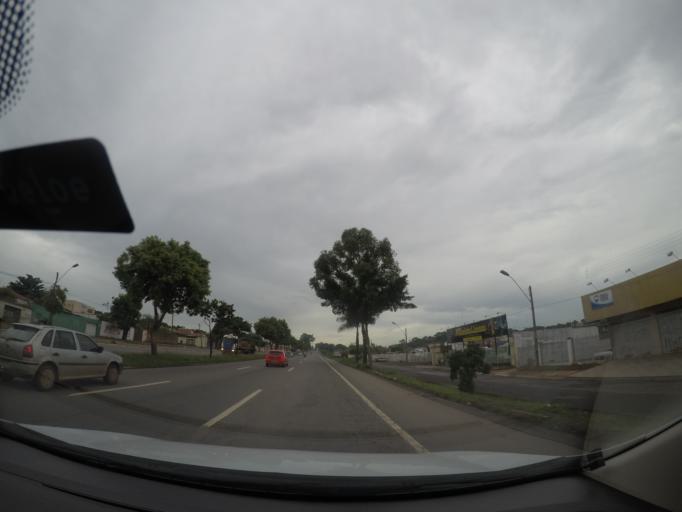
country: BR
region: Goias
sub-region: Goiania
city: Goiania
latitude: -16.6386
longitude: -49.2846
